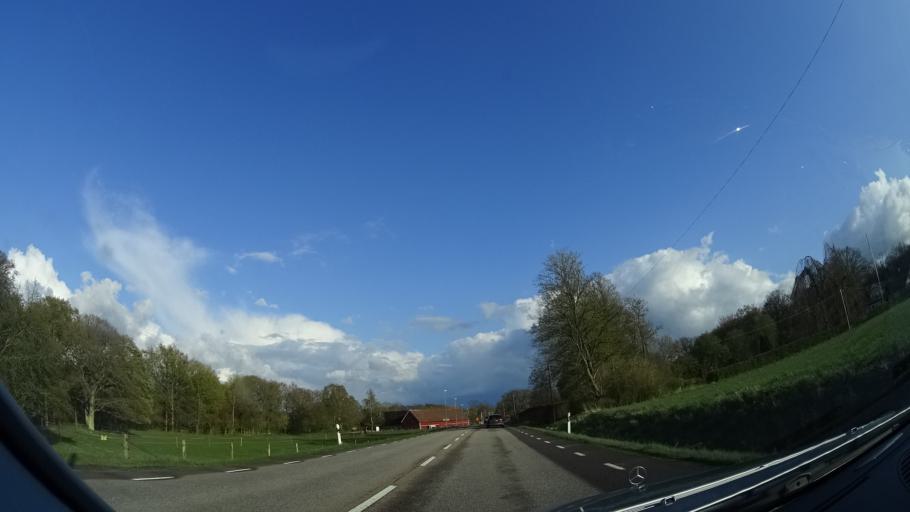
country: SE
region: Skane
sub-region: Klippans Kommun
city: Ljungbyhed
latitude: 56.0062
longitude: 13.2866
